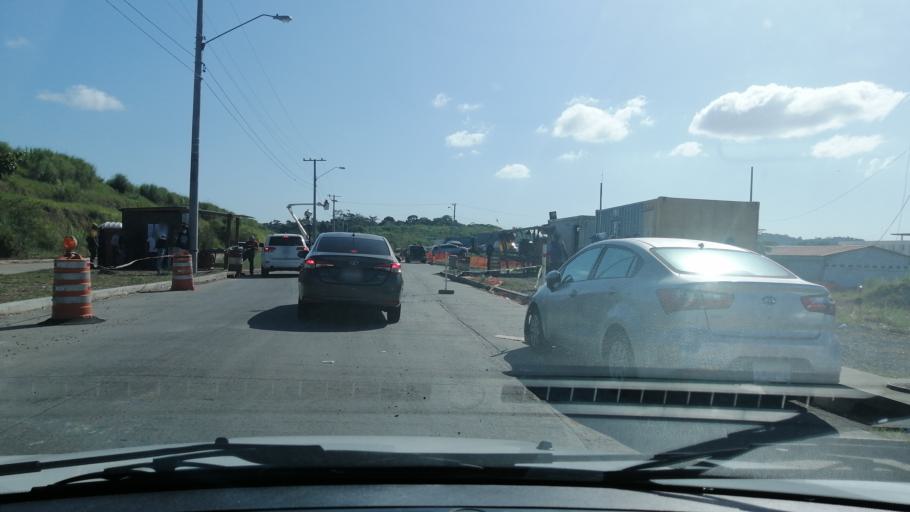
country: PA
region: Panama
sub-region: Distrito de Panama
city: Paraiso
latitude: 9.0274
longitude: -79.5804
